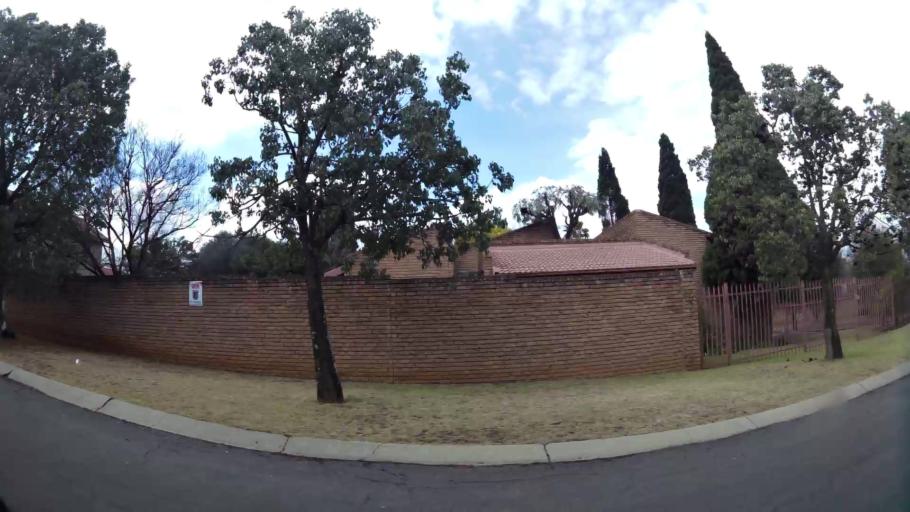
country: ZA
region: Gauteng
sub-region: Sedibeng District Municipality
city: Vanderbijlpark
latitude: -26.7416
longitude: 27.8515
